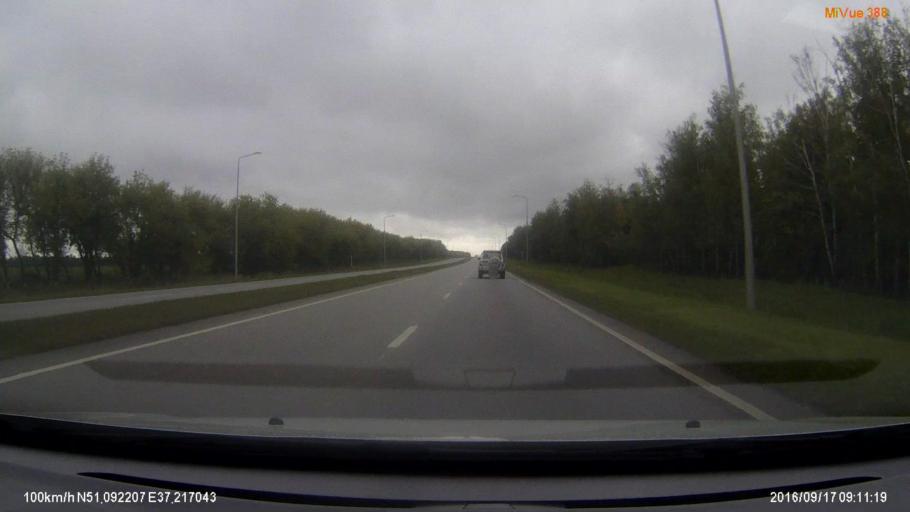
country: RU
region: Belgorod
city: Skorodnoye
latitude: 51.0919
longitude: 37.2169
